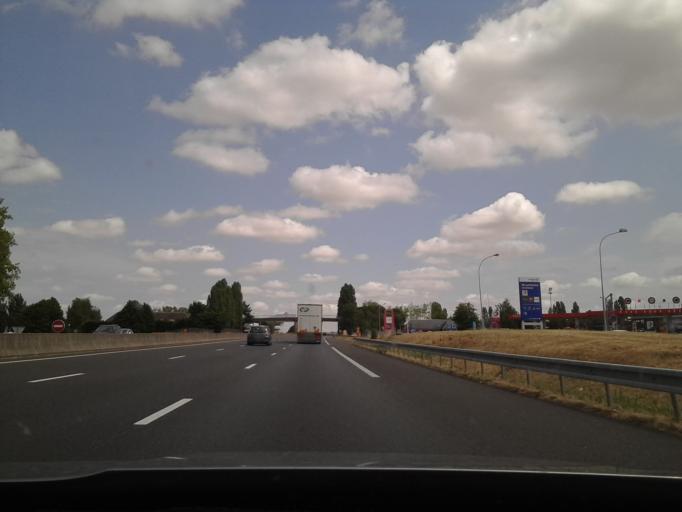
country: FR
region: Centre
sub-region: Departement d'Indre-et-Loire
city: Monnaie
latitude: 47.4730
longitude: 0.7738
